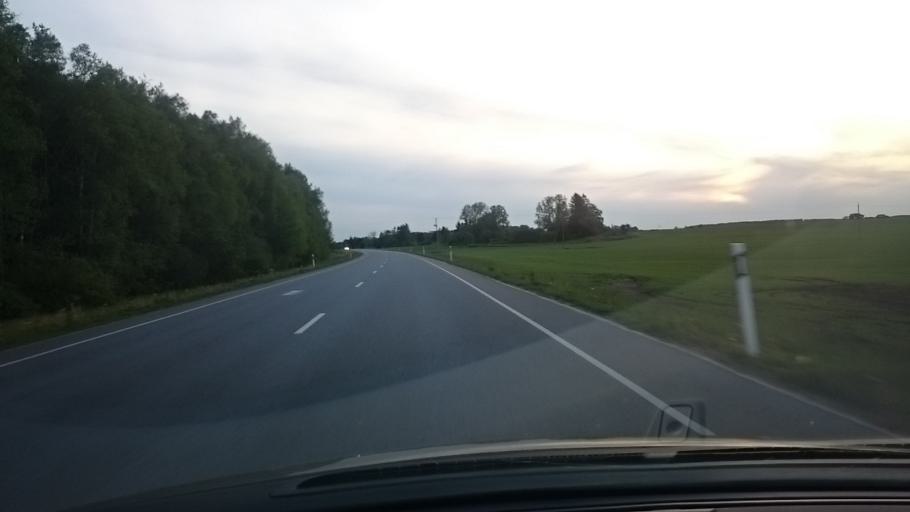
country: EE
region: Jaervamaa
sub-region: Tueri vald
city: Sarevere
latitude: 58.7779
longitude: 25.5000
